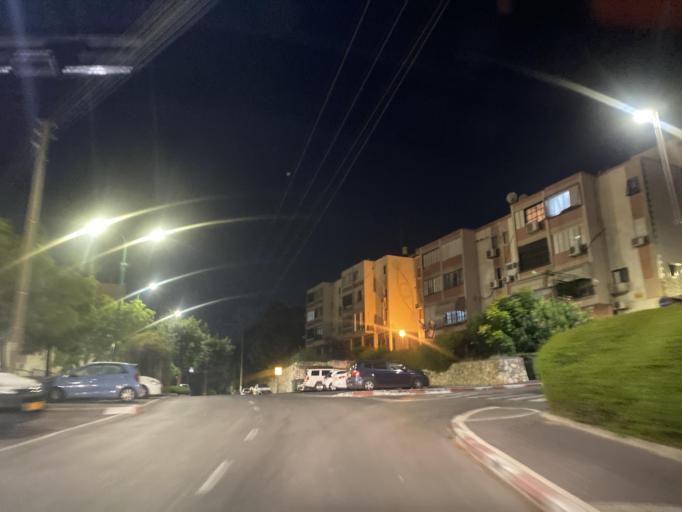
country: IL
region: Haifa
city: Daliyat el Karmil
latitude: 32.6559
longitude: 35.1040
